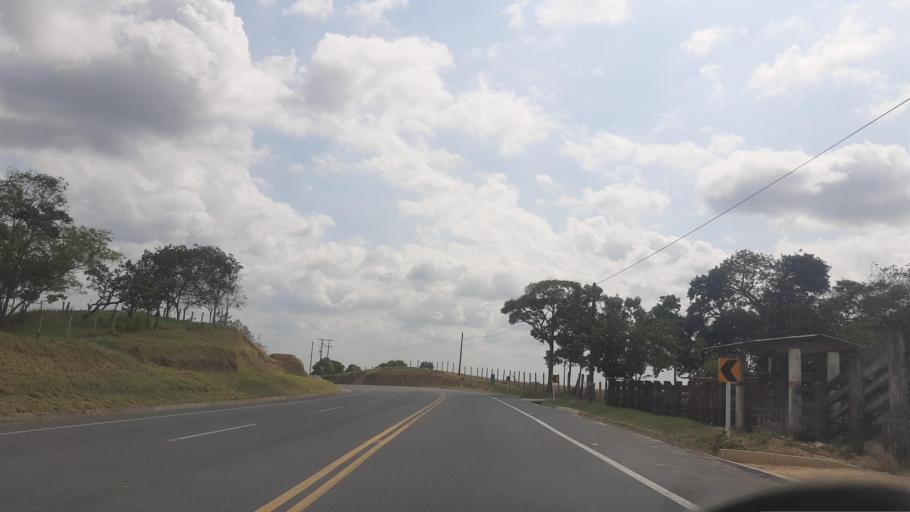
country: CO
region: Casanare
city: Monterrey
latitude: 4.8393
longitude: -72.8361
